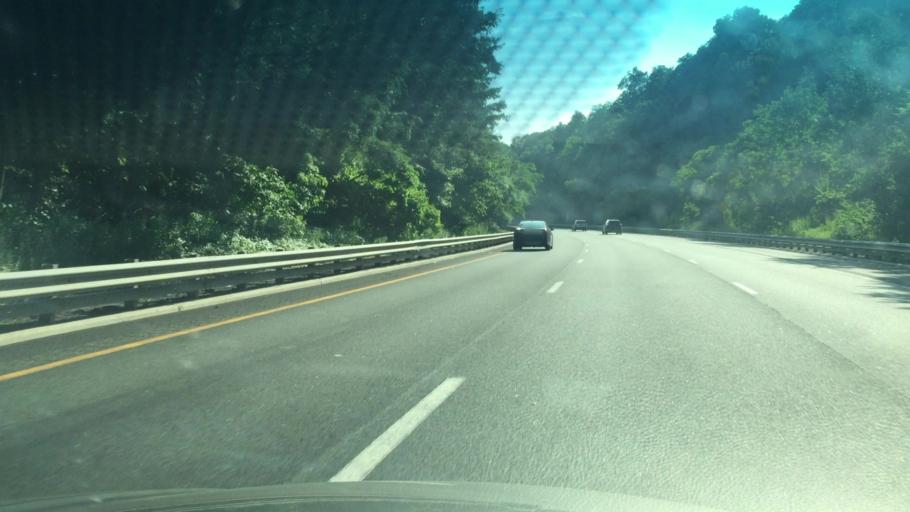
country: US
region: New Jersey
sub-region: Warren County
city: Hackettstown
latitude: 40.9234
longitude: -74.7987
